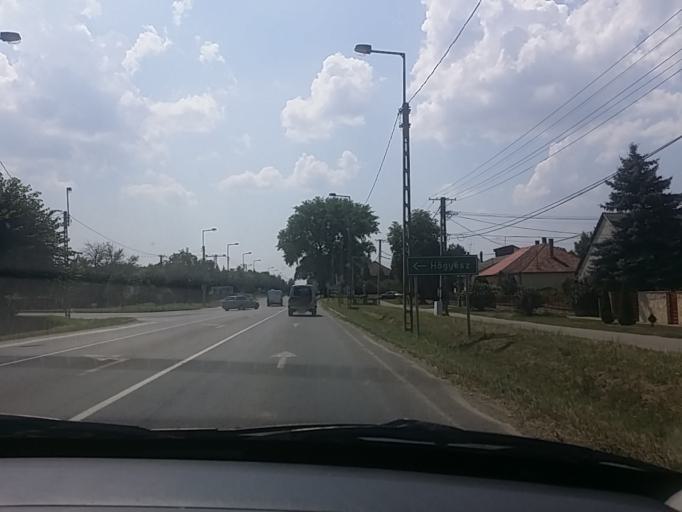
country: HU
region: Tolna
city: Dombovar
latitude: 46.3961
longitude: 18.1478
